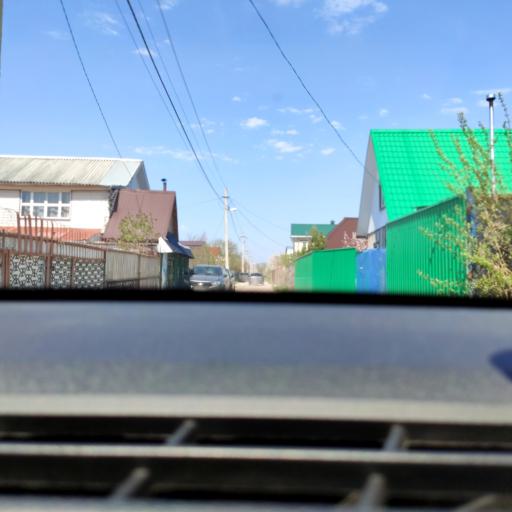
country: RU
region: Samara
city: Tol'yatti
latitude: 53.5916
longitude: 49.3004
